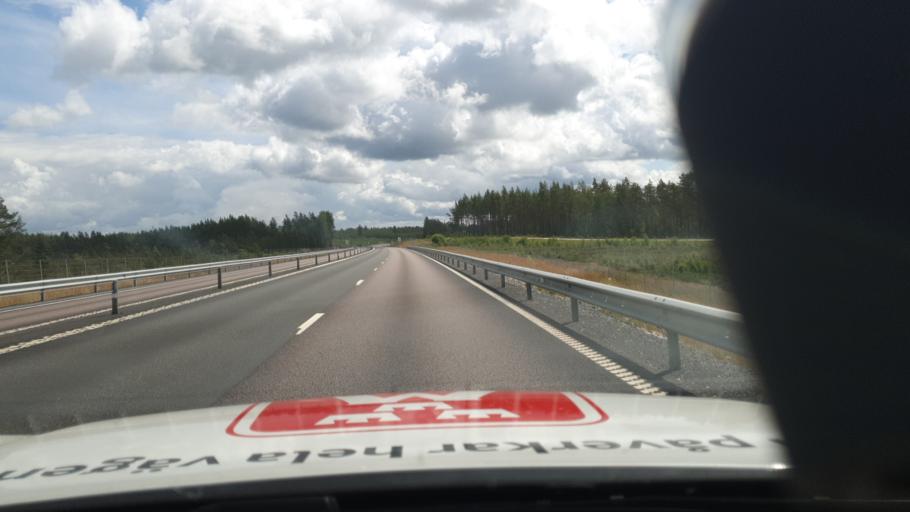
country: SE
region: Joenkoeping
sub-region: Mullsjo Kommun
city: Mullsjoe
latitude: 57.8660
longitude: 13.9729
